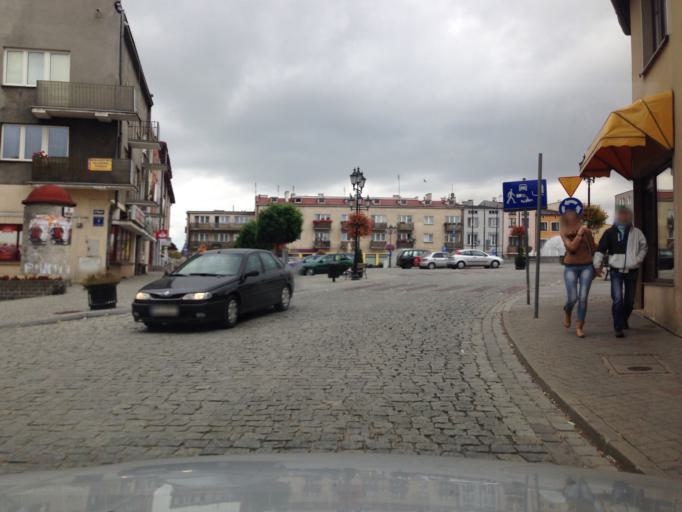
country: PL
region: Warmian-Masurian Voivodeship
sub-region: Powiat ilawski
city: Lubawa
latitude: 53.5036
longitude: 19.7495
